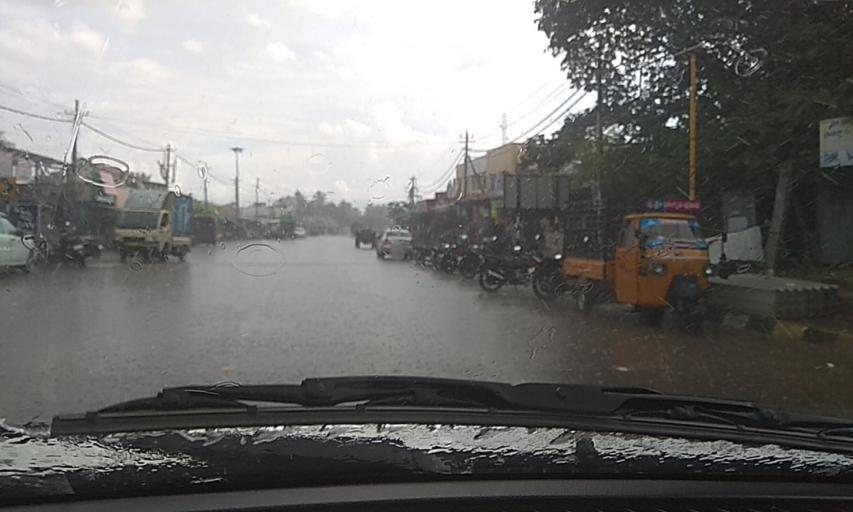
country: IN
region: Karnataka
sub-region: Mandya
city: Maddur
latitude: 12.6930
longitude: 77.0604
